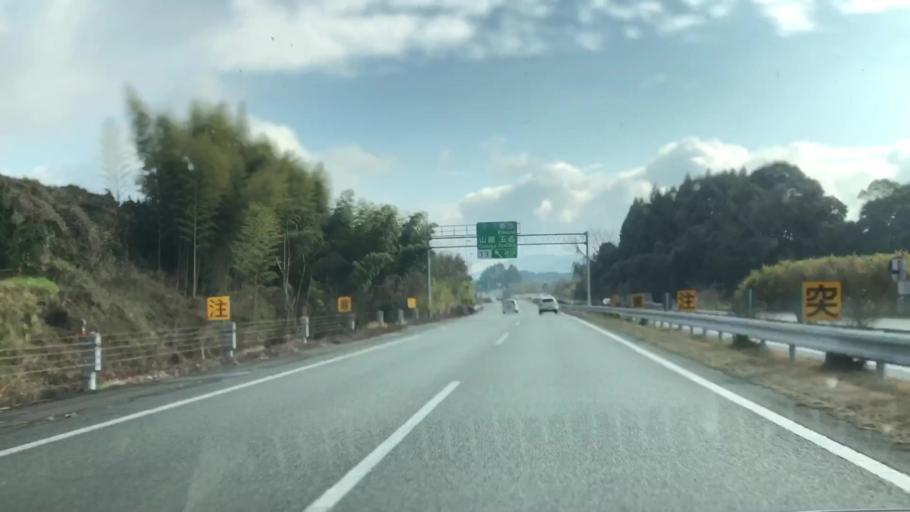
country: JP
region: Kumamoto
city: Tamana
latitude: 32.9902
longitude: 130.6032
